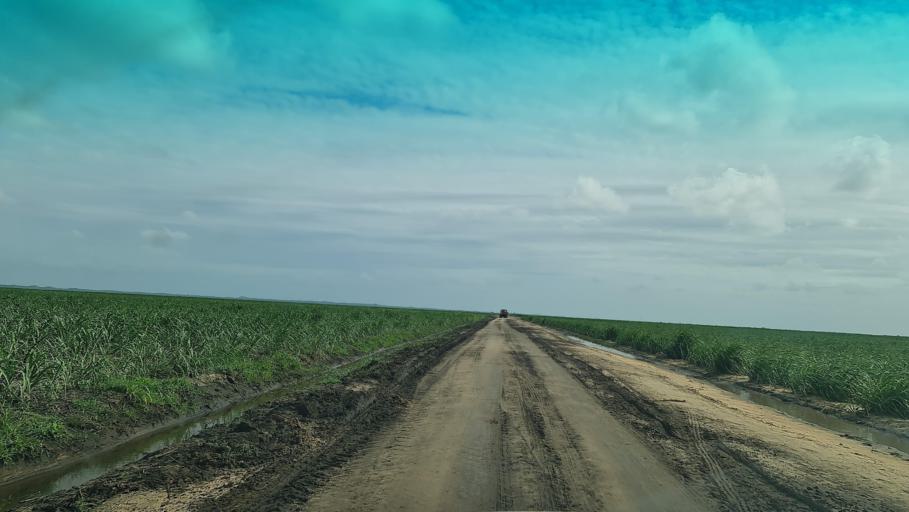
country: MZ
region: Maputo
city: Manhica
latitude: -25.4749
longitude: 32.8168
